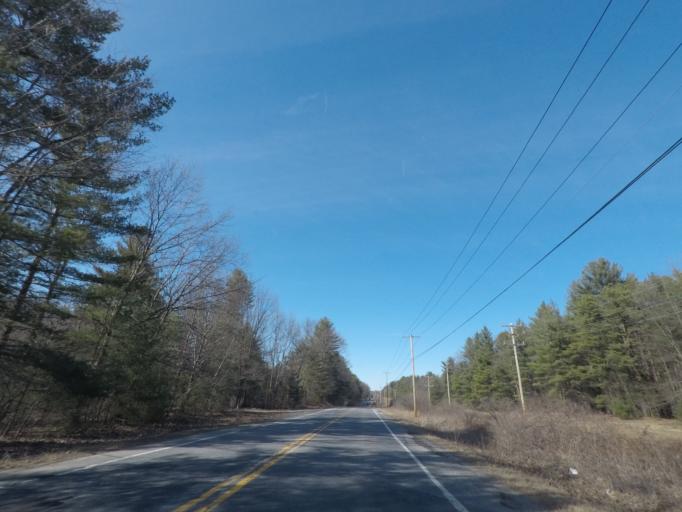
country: US
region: New York
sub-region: Saratoga County
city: Milton
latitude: 43.0507
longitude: -73.8506
